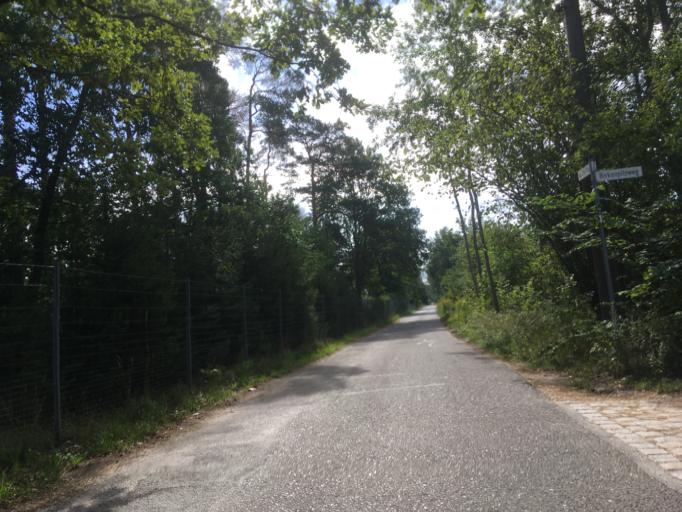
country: DE
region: Brandenburg
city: Oranienburg
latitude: 52.7623
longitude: 13.3294
